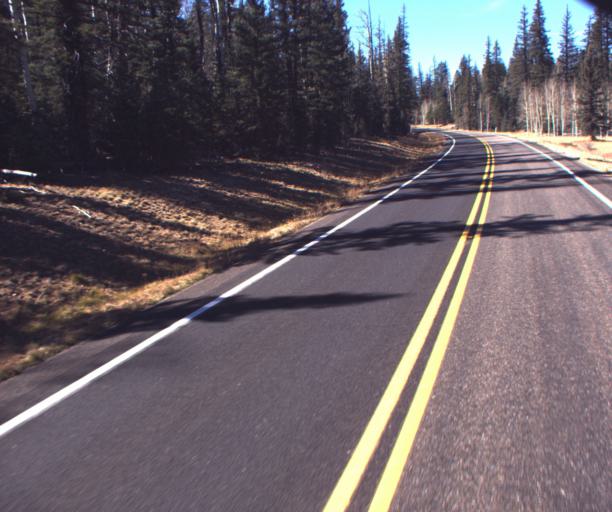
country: US
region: Arizona
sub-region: Coconino County
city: Grand Canyon
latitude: 36.5238
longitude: -112.1422
